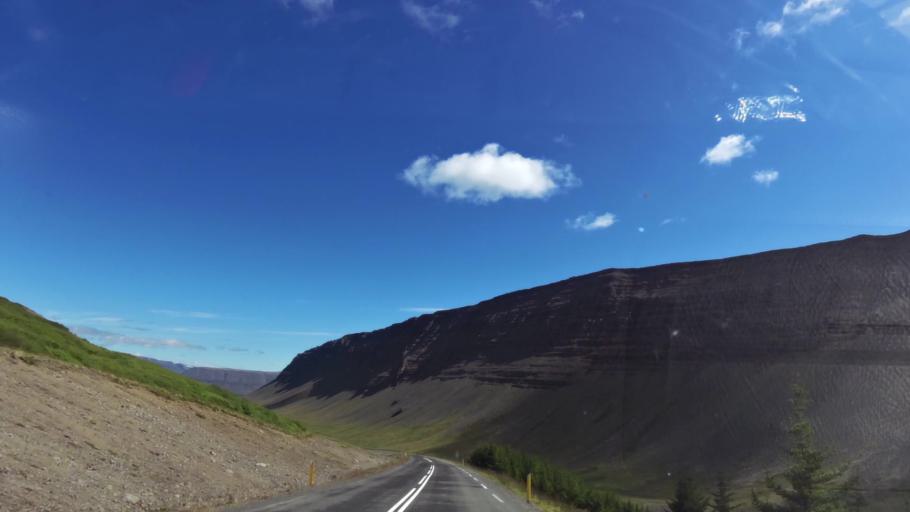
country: IS
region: Westfjords
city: Isafjoerdur
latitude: 65.6601
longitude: -23.6451
